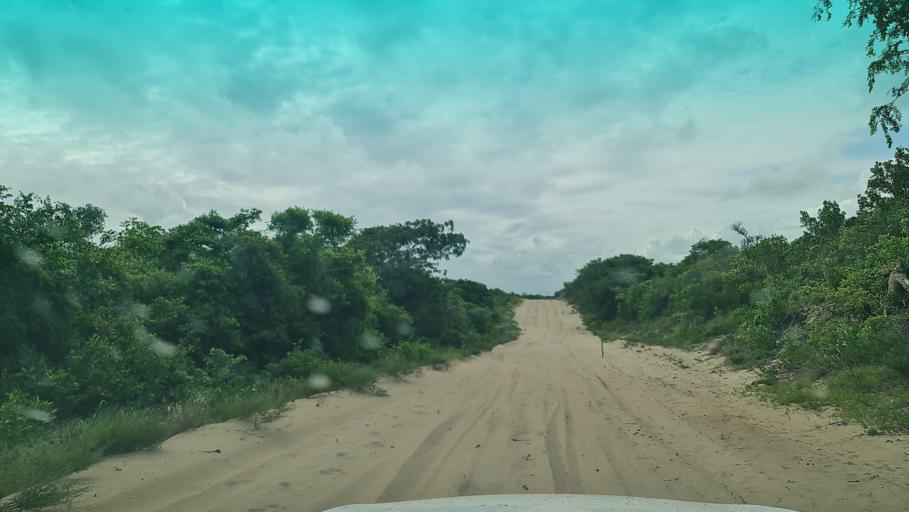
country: MZ
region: Maputo
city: Manhica
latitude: -25.4352
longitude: 32.9108
